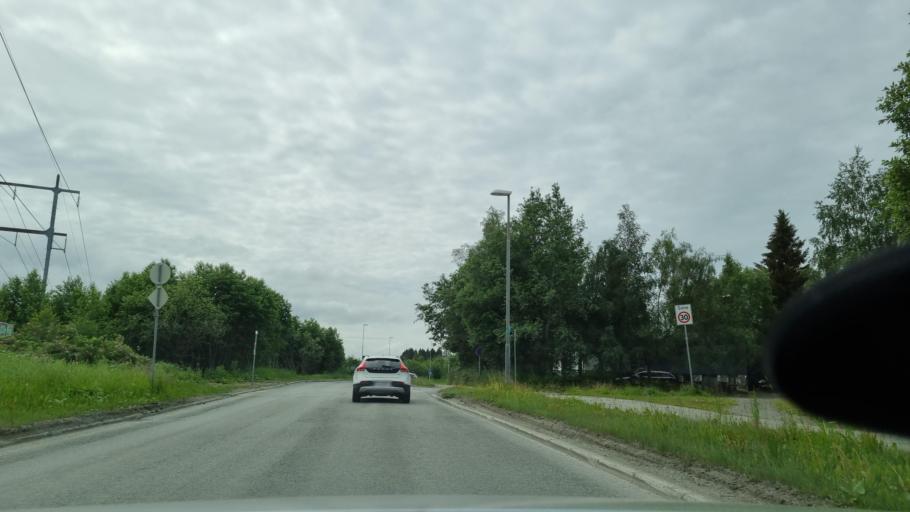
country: NO
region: Sor-Trondelag
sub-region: Melhus
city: Melhus
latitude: 63.3480
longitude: 10.3477
